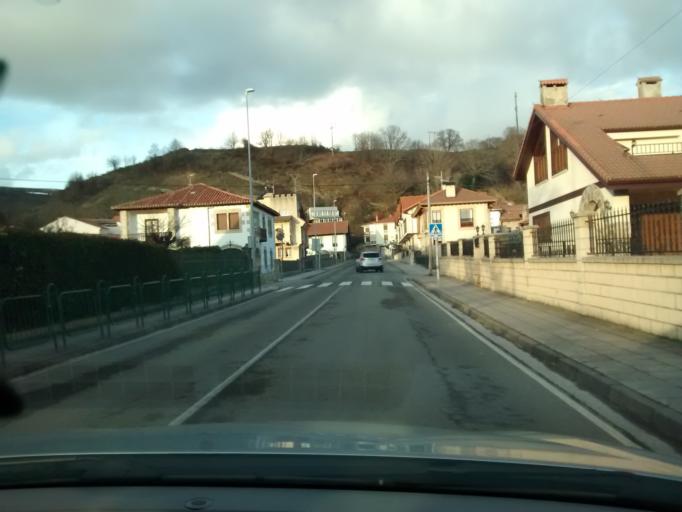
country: ES
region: Castille and Leon
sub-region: Provincia de Burgos
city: Espinosa de los Monteros
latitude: 43.0776
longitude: -3.5546
